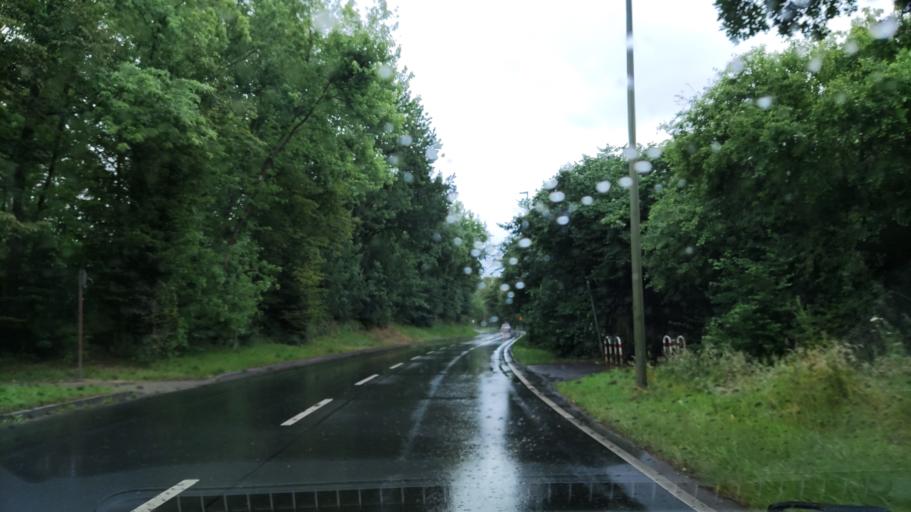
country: DE
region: North Rhine-Westphalia
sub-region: Regierungsbezirk Arnsberg
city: Hamm
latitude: 51.7028
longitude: 7.8411
